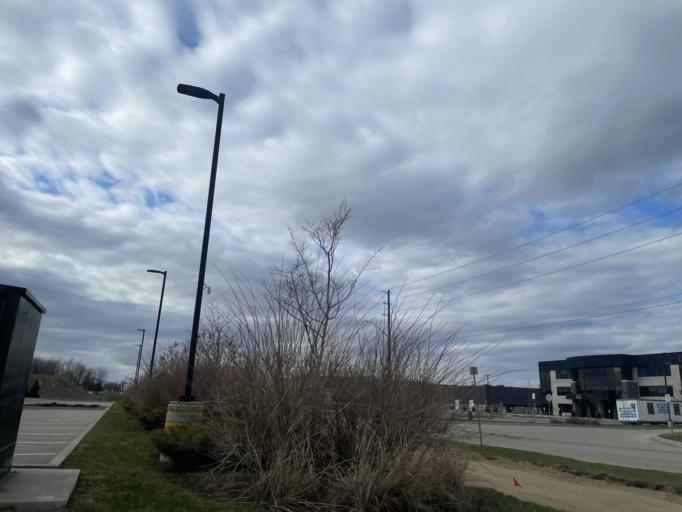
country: CA
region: Ontario
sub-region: Wellington County
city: Guelph
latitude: 43.4916
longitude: -80.2192
